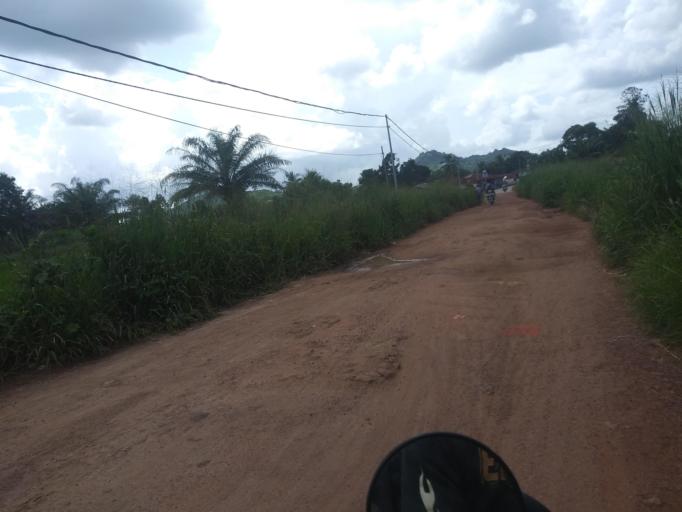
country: SL
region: Northern Province
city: Makeni
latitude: 8.8772
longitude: -12.0425
